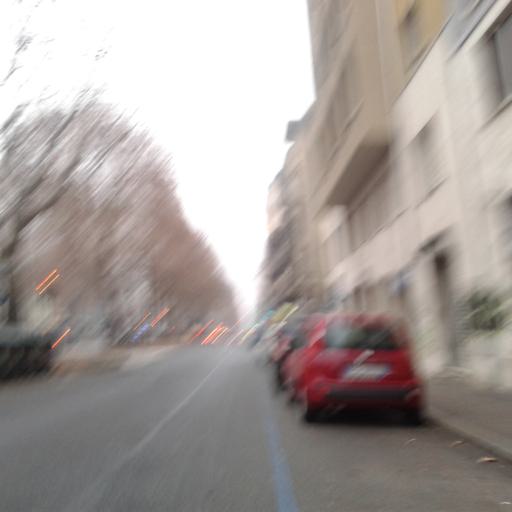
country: IT
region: Piedmont
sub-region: Provincia di Torino
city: Turin
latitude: 45.0798
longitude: 7.6741
